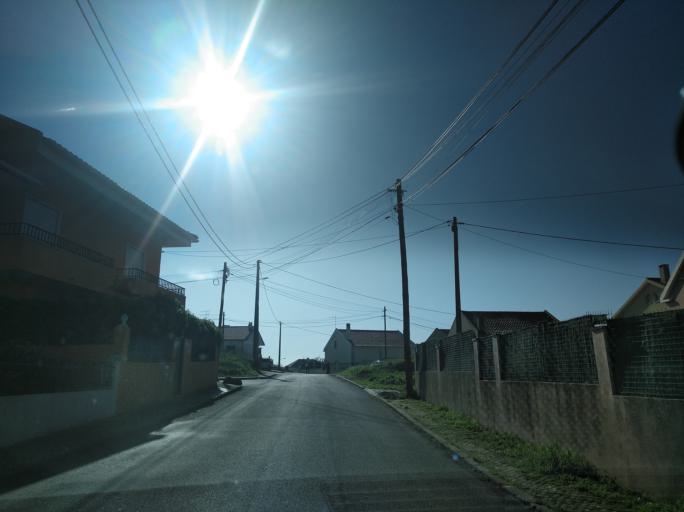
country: PT
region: Lisbon
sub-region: Odivelas
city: Canecas
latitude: 38.8034
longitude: -9.2198
